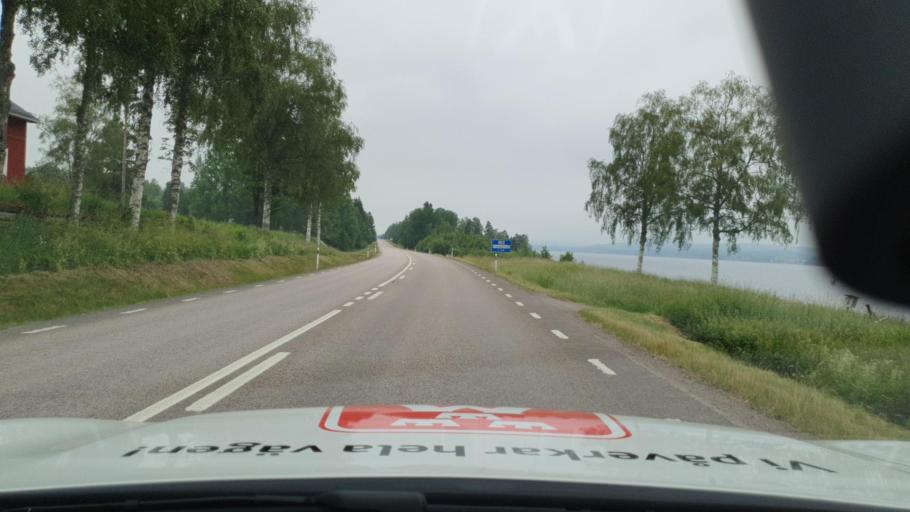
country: SE
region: Vaermland
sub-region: Sunne Kommun
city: Sunne
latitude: 59.8768
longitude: 13.1420
